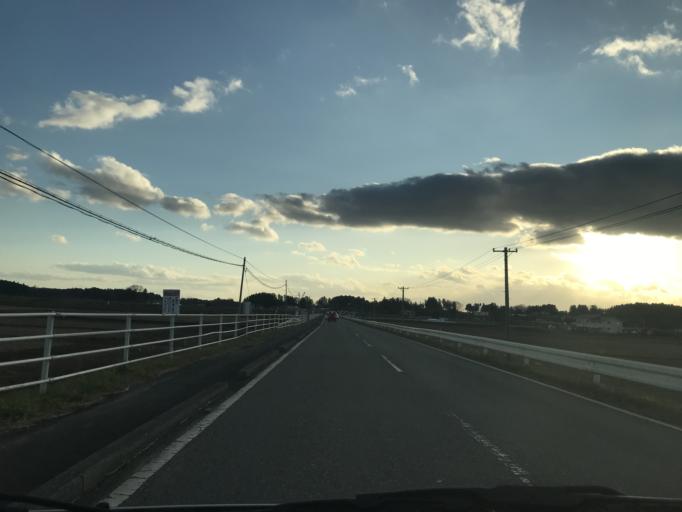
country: JP
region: Miyagi
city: Kogota
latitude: 38.6411
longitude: 141.0722
